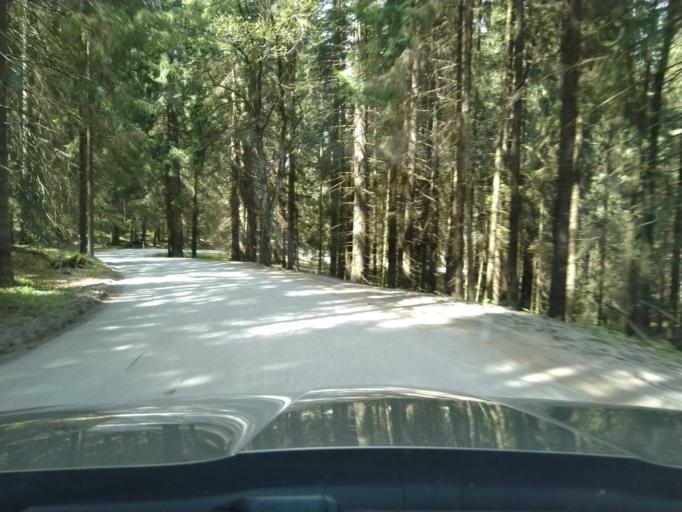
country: CZ
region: Jihocesky
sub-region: Okres Prachatice
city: Vimperk
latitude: 49.0158
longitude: 13.7274
